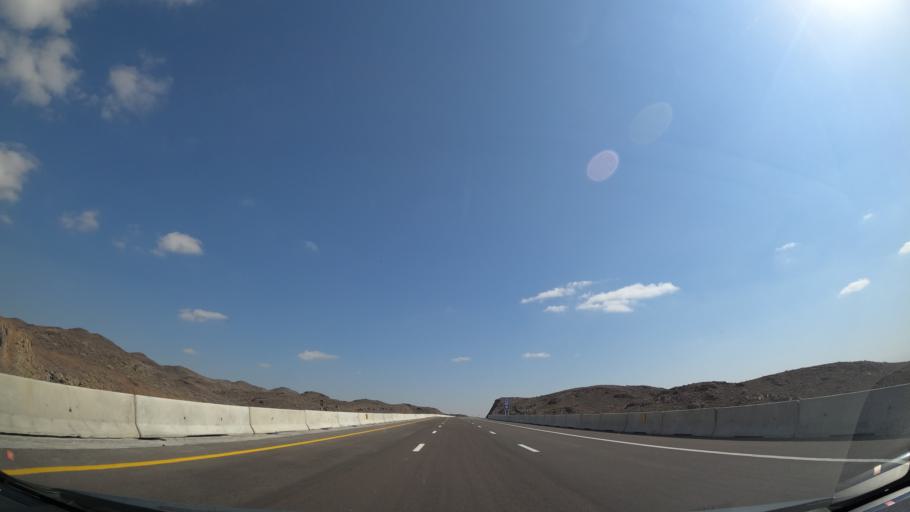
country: IR
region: Alborz
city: Eshtehard
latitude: 35.6613
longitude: 50.6559
